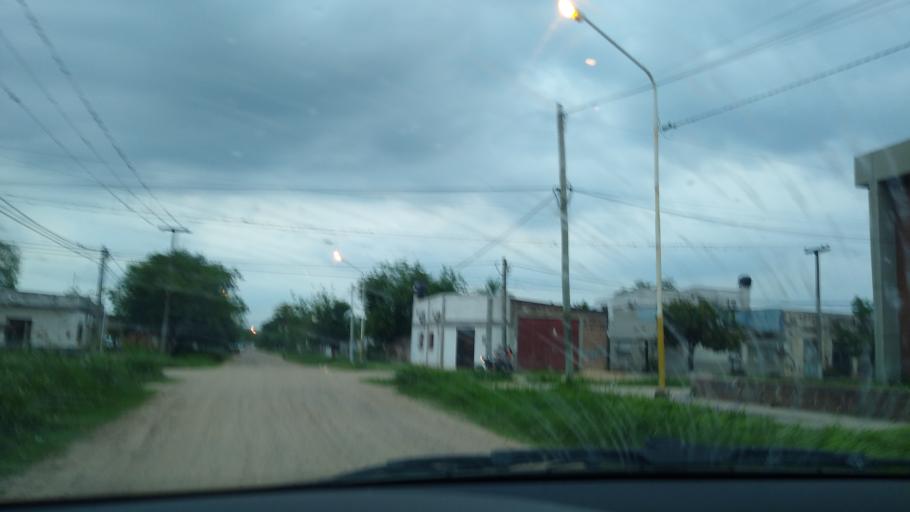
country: AR
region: Chaco
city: Barranqueras
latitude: -27.4882
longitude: -58.9355
